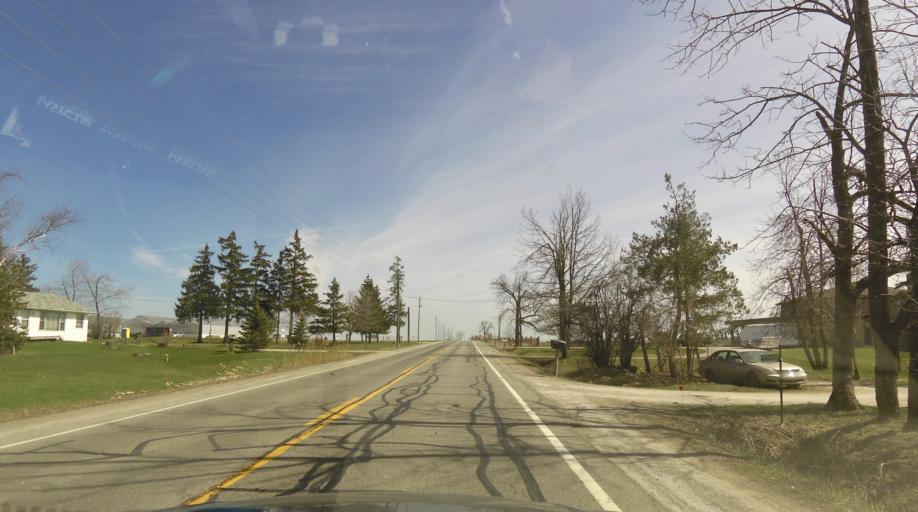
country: CA
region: Ontario
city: Brampton
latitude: 43.6978
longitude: -79.8715
